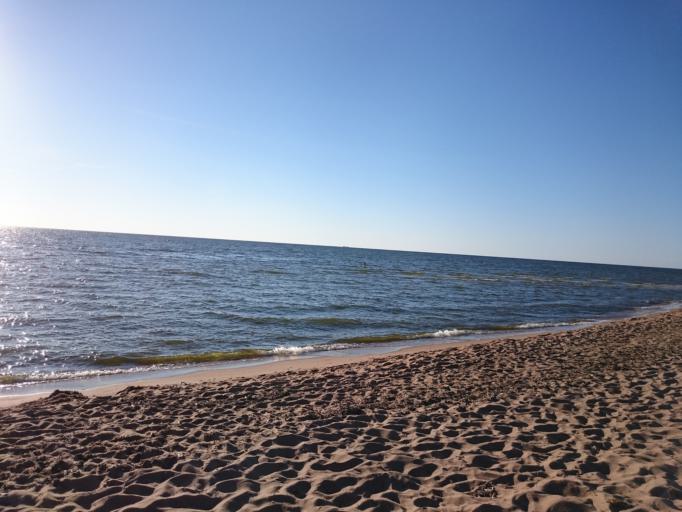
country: LV
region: Saulkrastu
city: Saulkrasti
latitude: 57.2715
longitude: 24.4119
